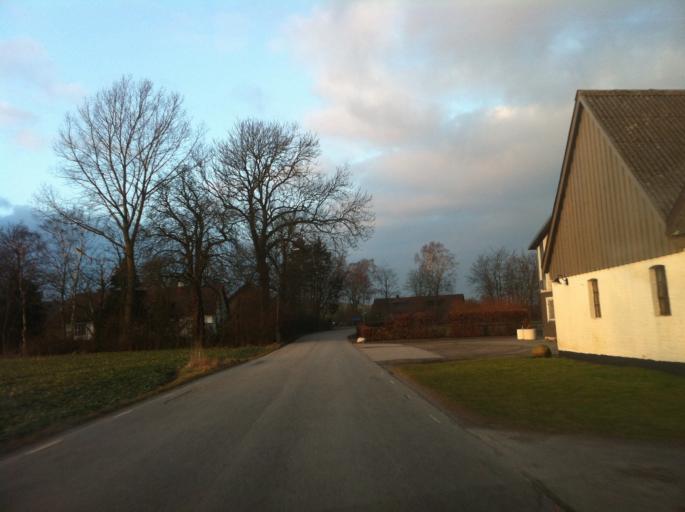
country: SE
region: Skane
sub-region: Kavlinge Kommun
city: Loddekopinge
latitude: 55.8056
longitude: 13.0398
